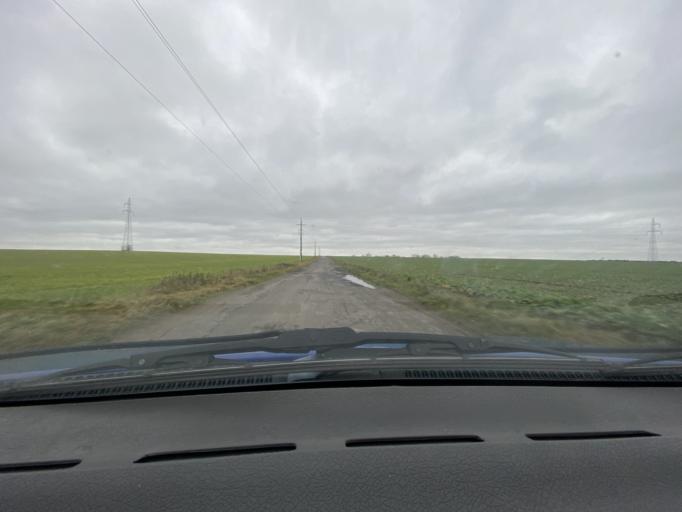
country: PL
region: West Pomeranian Voivodeship
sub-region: Powiat gryficki
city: Gryfice
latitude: 53.9550
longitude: 15.2578
